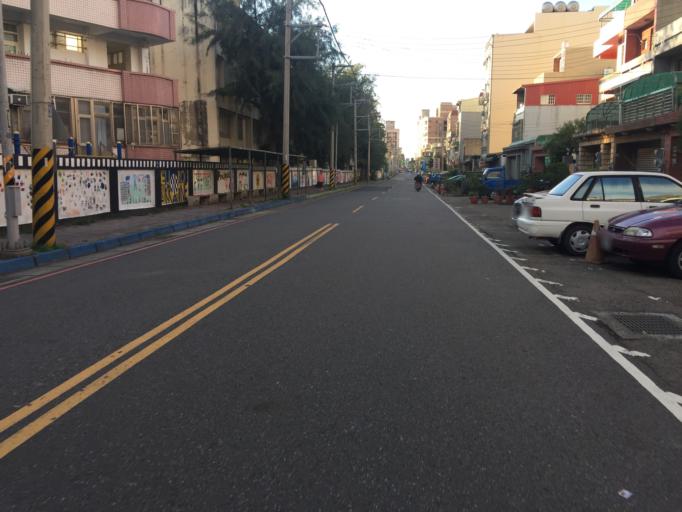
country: TW
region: Taiwan
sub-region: Hsinchu
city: Hsinchu
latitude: 24.8131
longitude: 120.9829
